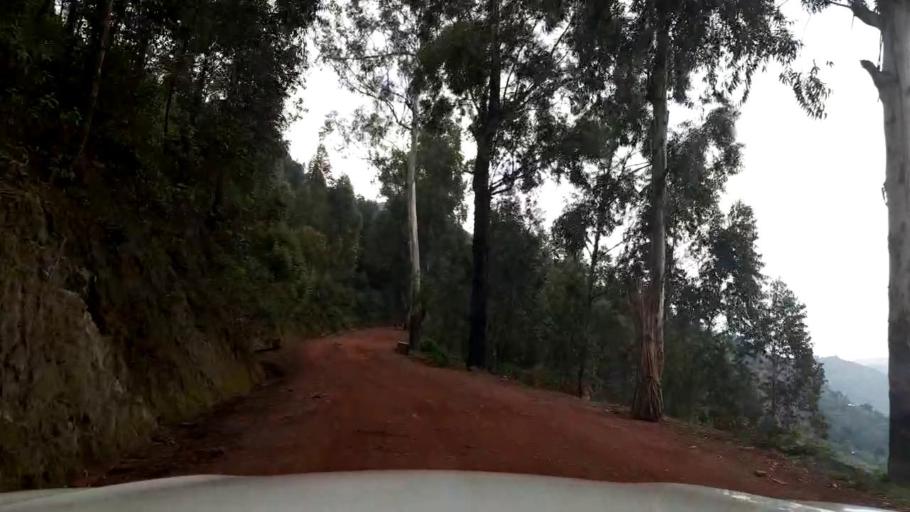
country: UG
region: Western Region
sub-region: Kisoro District
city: Kisoro
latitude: -1.4057
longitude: 29.8009
